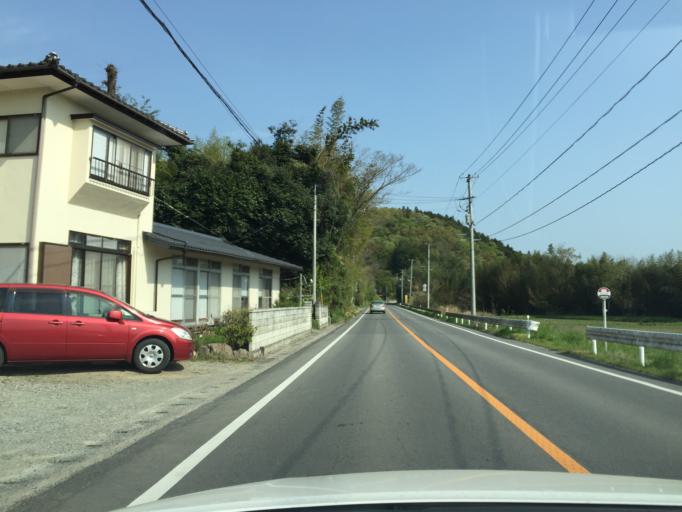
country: JP
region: Fukushima
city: Iwaki
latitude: 37.1282
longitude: 140.8689
